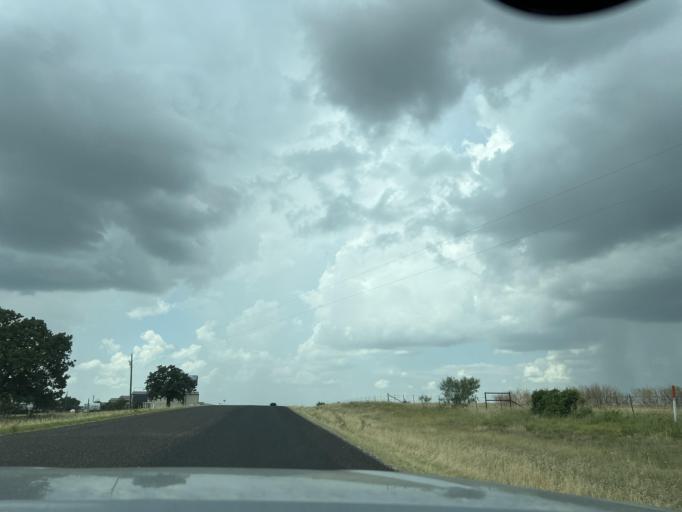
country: US
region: Texas
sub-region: Wise County
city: Decatur
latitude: 33.1765
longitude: -97.6209
